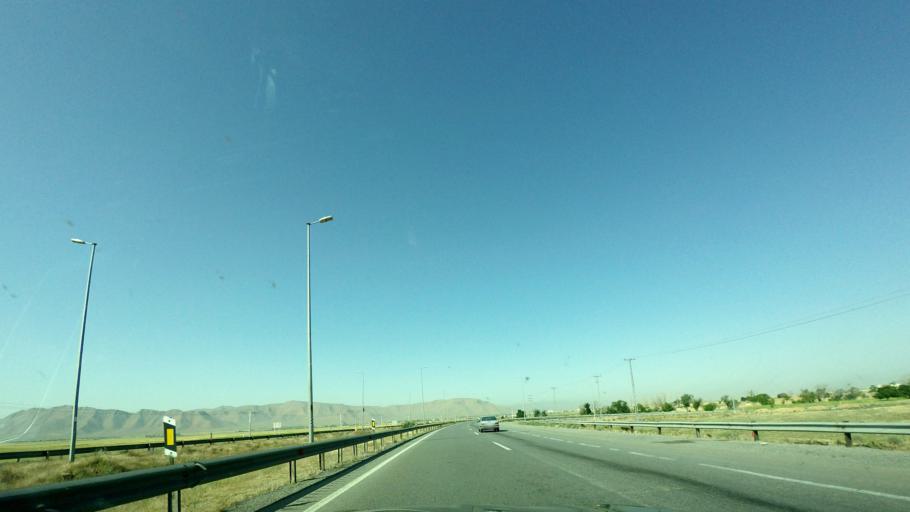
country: IR
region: Markazi
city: Arak
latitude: 34.1688
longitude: 50.0327
